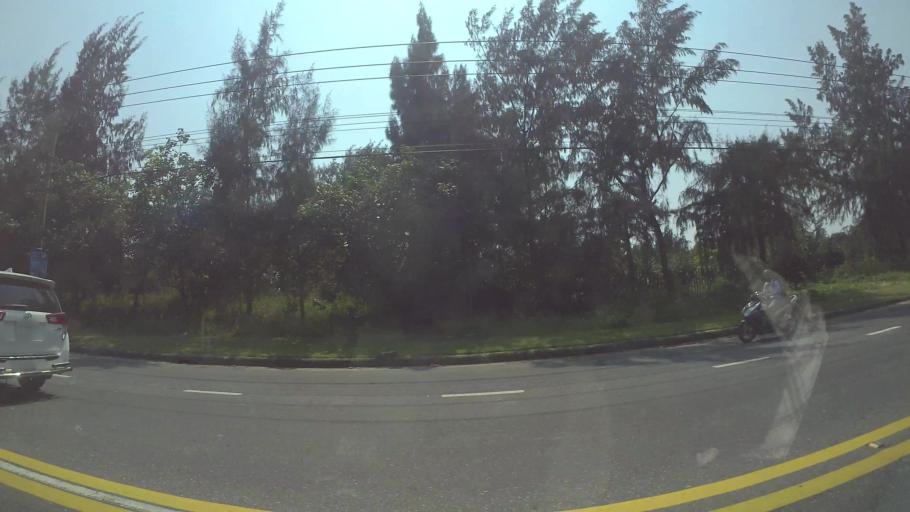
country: VN
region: Da Nang
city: Ngu Hanh Son
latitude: 15.9767
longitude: 108.2781
